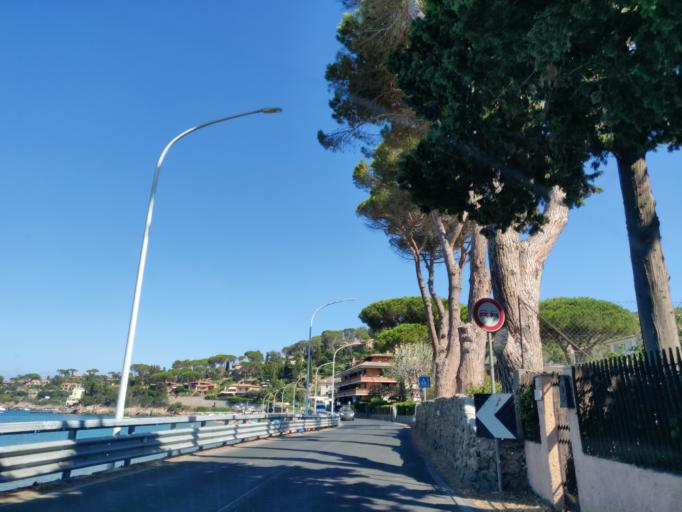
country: IT
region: Tuscany
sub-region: Provincia di Grosseto
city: Monte Argentario
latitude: 42.4341
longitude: 11.1391
